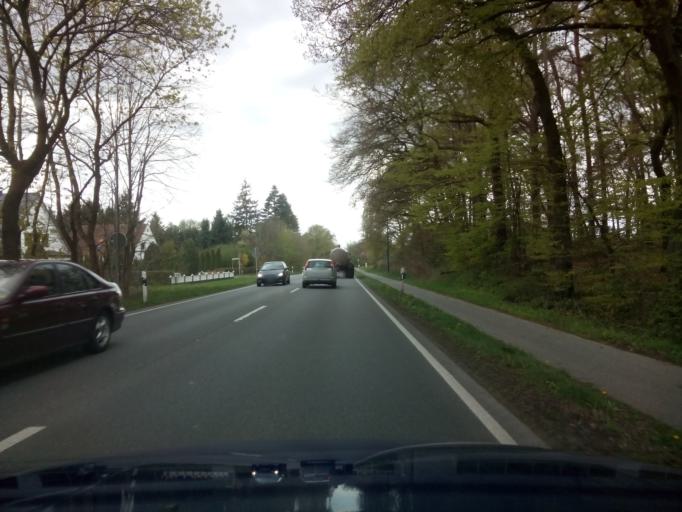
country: DE
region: Lower Saxony
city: Hambergen
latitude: 53.2808
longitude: 8.8230
